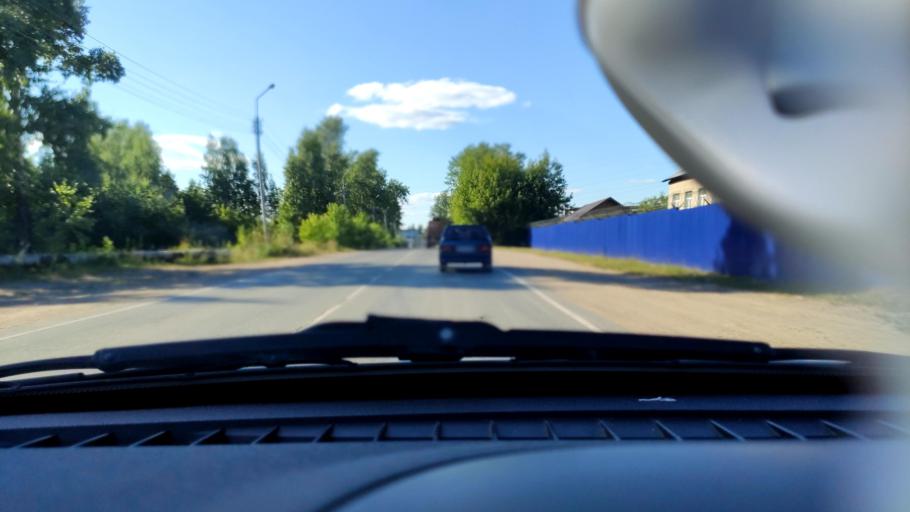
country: RU
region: Perm
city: Krasnokamsk
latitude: 58.0766
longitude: 55.7886
